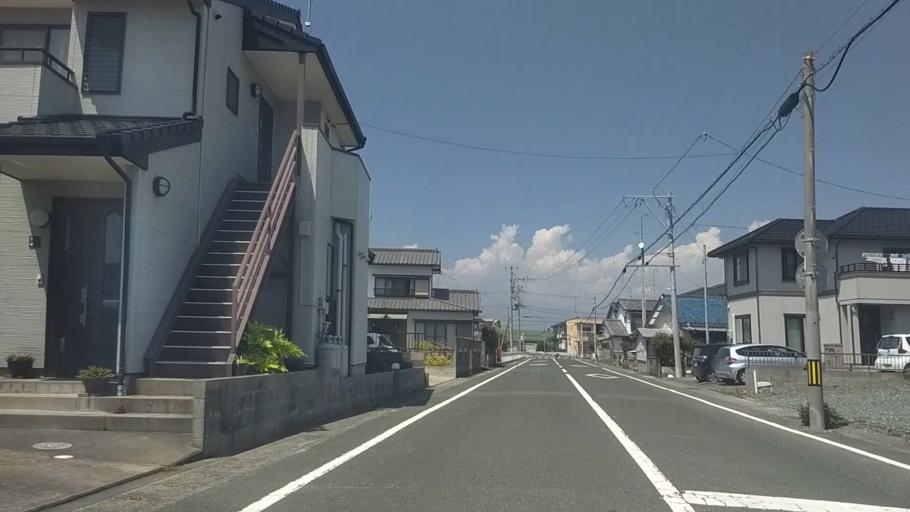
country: JP
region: Shizuoka
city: Kosai-shi
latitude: 34.6837
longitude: 137.5777
